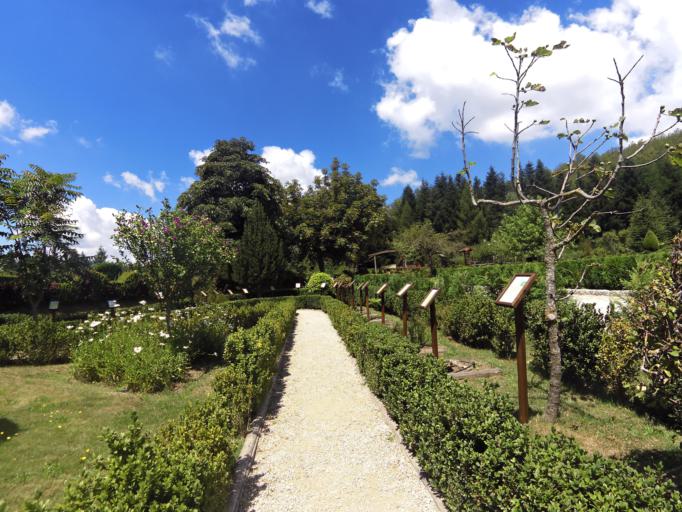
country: IT
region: Calabria
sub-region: Provincia di Vibo-Valentia
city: Mongiana
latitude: 38.5160
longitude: 16.3165
